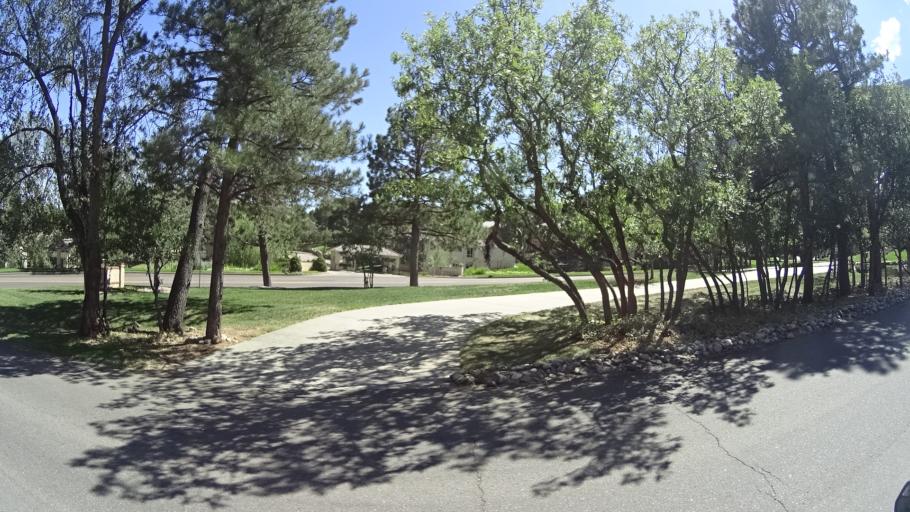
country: US
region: Colorado
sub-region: El Paso County
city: Colorado Springs
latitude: 38.7786
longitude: -104.8555
